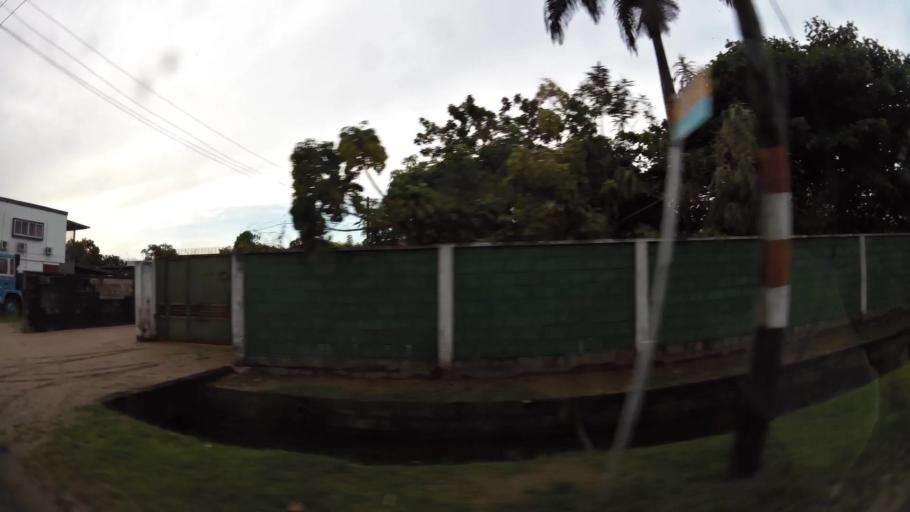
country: SR
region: Paramaribo
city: Paramaribo
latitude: 5.8275
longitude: -55.1862
